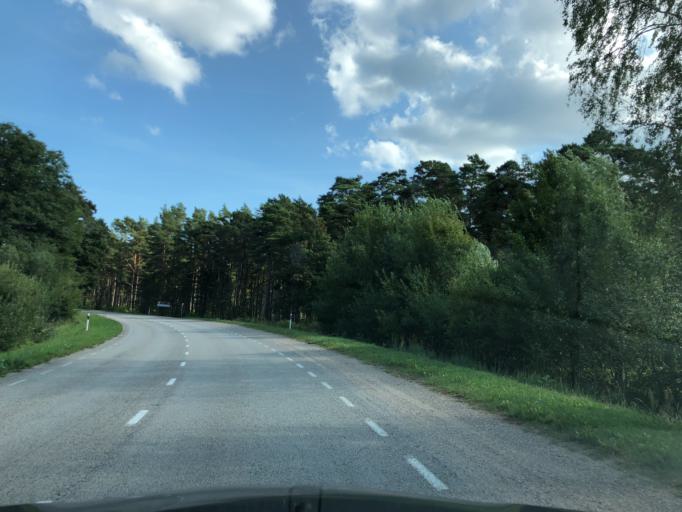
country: EE
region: Hiiumaa
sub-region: Kaerdla linn
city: Kardla
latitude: 58.7082
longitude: 22.5886
